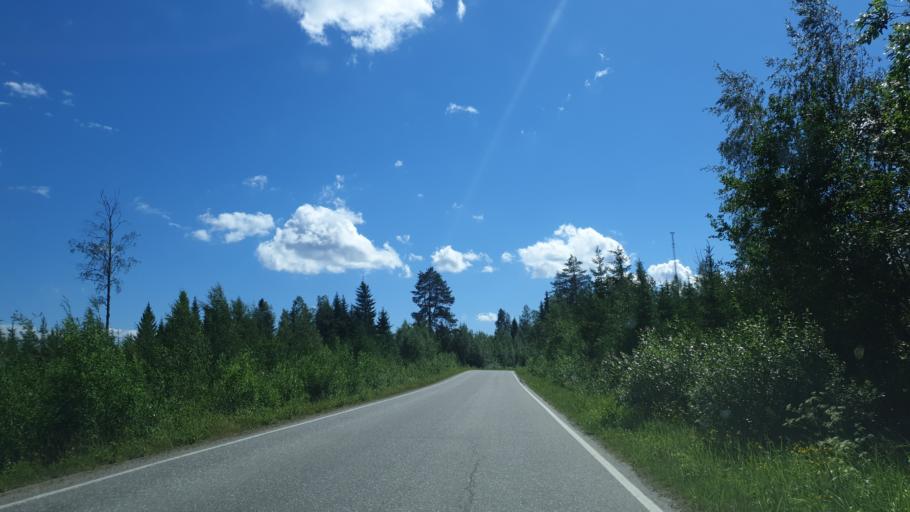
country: FI
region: Northern Savo
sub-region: Koillis-Savo
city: Kaavi
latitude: 62.9956
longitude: 28.5045
